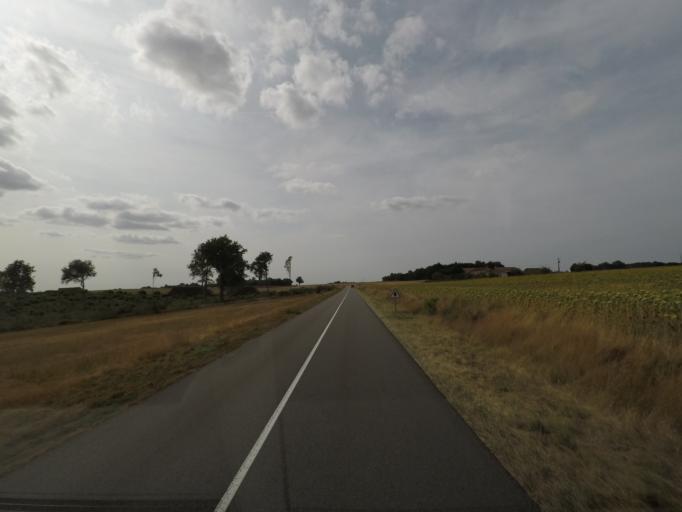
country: FR
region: Poitou-Charentes
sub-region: Departement de la Charente
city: Ruffec
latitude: 46.0223
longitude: 0.2599
